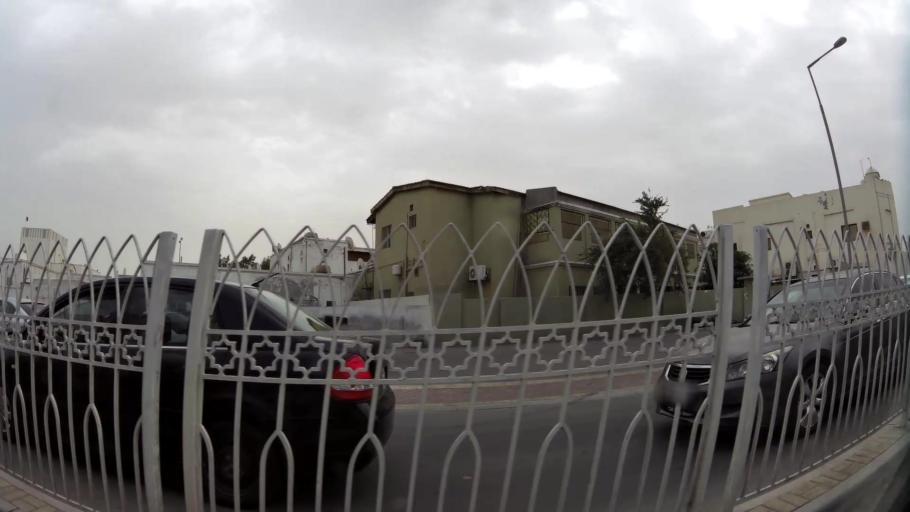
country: BH
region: Northern
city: Ar Rifa'
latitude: 26.1272
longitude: 50.5466
